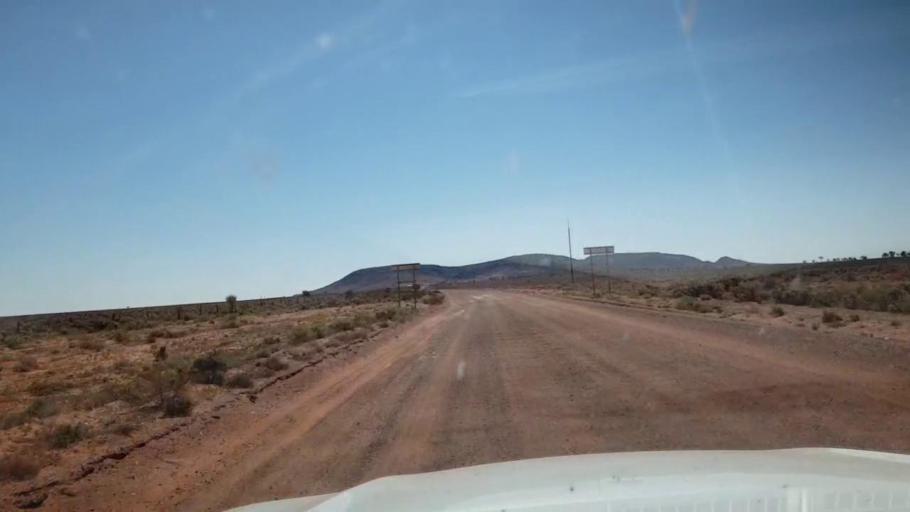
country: AU
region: South Australia
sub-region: Whyalla
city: Whyalla
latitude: -32.7133
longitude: 137.1418
